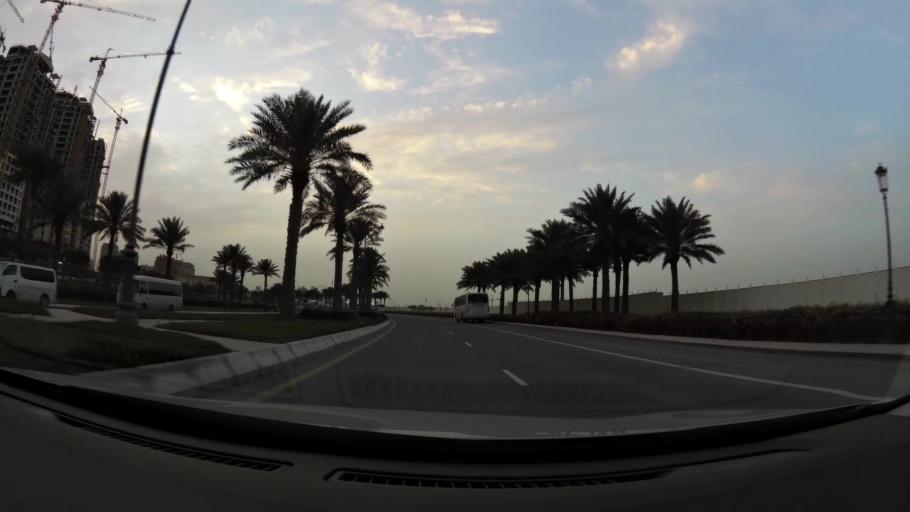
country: QA
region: Baladiyat ad Dawhah
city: Doha
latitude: 25.3699
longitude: 51.5608
